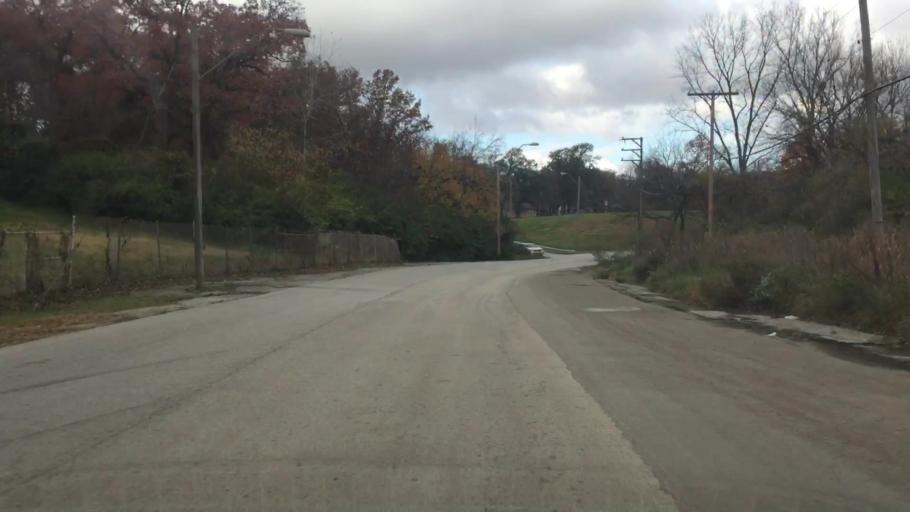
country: US
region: Kansas
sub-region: Johnson County
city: Leawood
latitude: 38.9898
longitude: -94.5423
